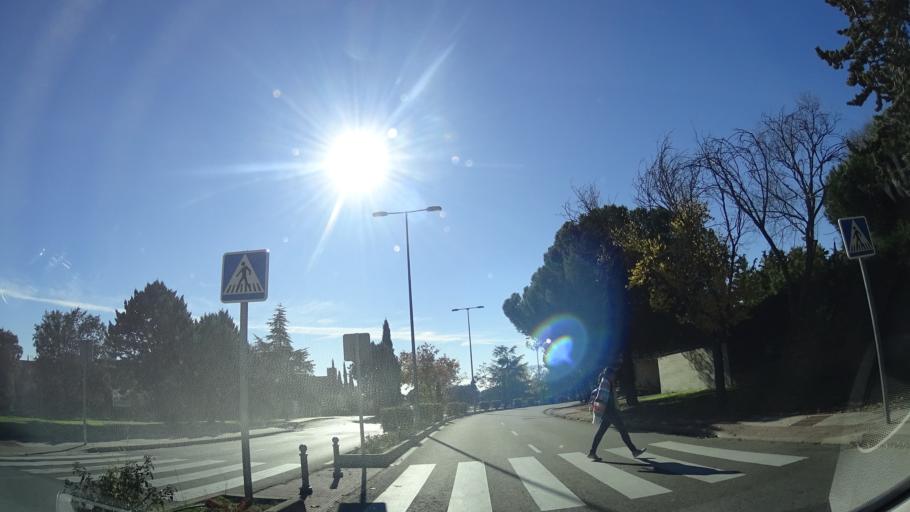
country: ES
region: Madrid
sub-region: Provincia de Madrid
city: Las Matas
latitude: 40.5349
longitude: -3.9013
